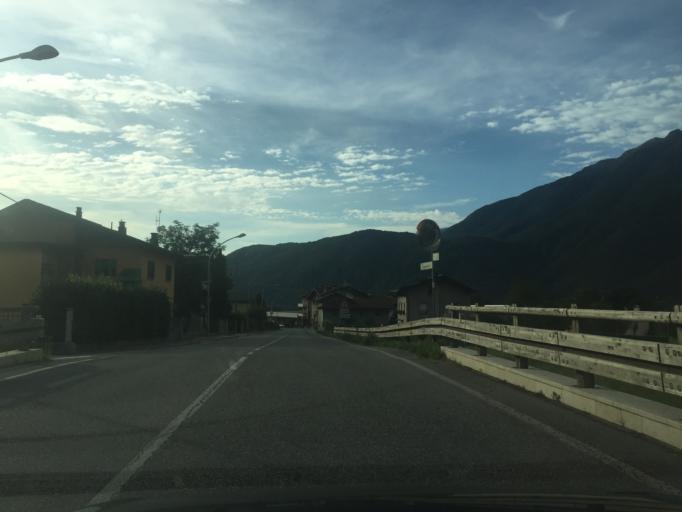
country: IT
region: Friuli Venezia Giulia
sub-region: Provincia di Udine
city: Villa Santina
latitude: 46.4195
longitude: 12.9115
